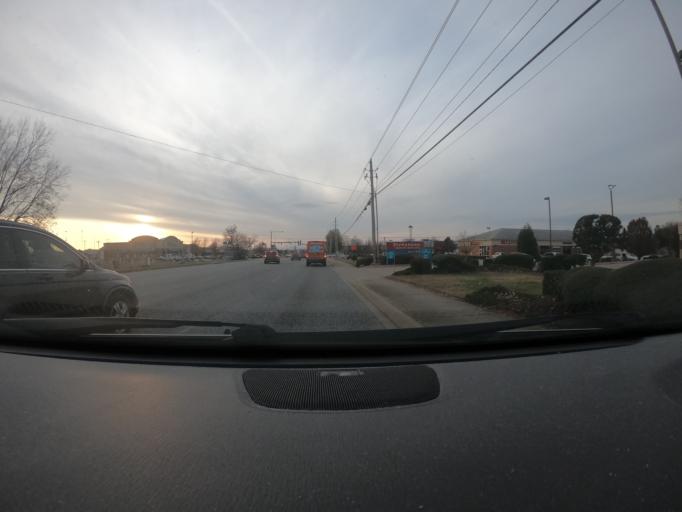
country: US
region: Arkansas
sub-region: Benton County
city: Bentonville
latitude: 36.3349
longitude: -94.1734
